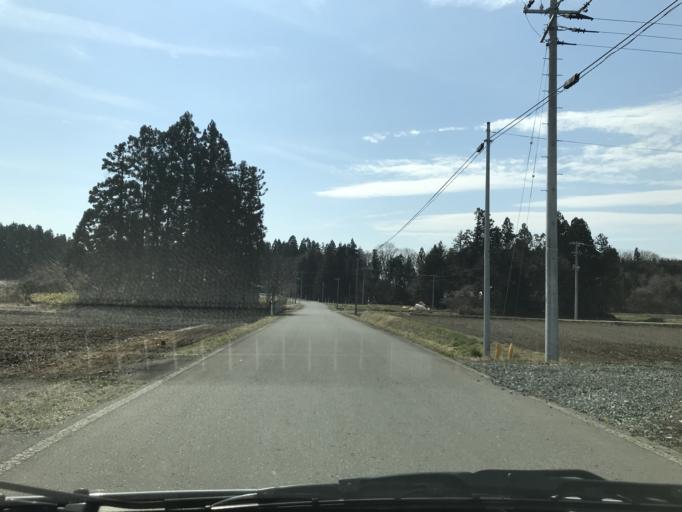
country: JP
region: Iwate
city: Mizusawa
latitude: 39.1204
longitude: 141.0433
